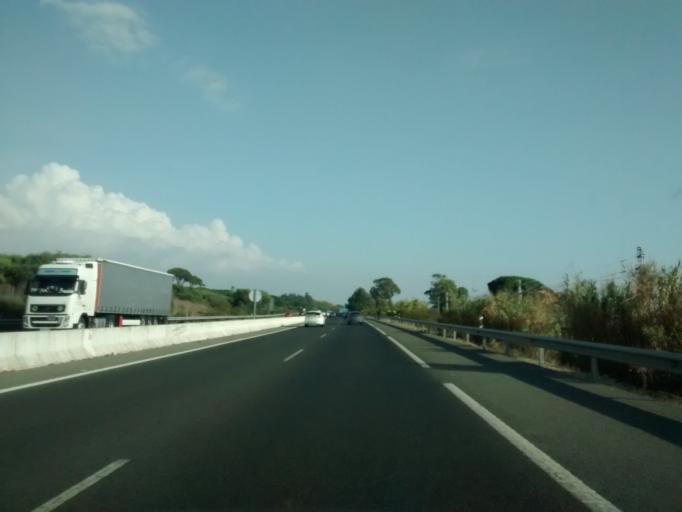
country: ES
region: Andalusia
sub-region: Provincia de Cadiz
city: Puerto Real
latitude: 36.5123
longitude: -6.1520
